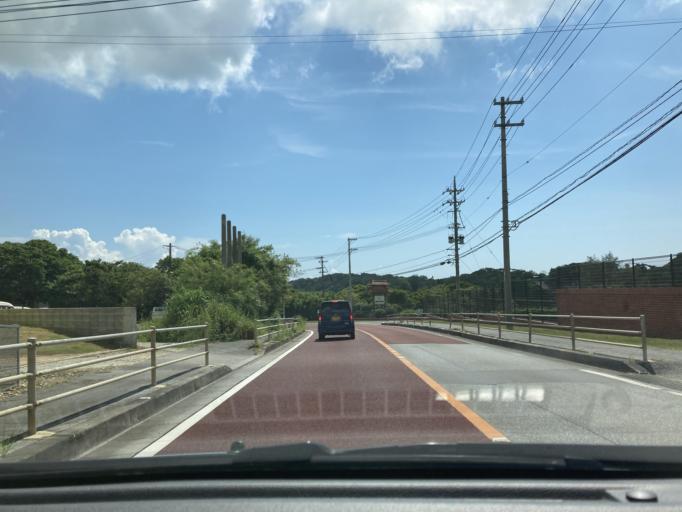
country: JP
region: Okinawa
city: Tomigusuku
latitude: 26.1524
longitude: 127.7773
